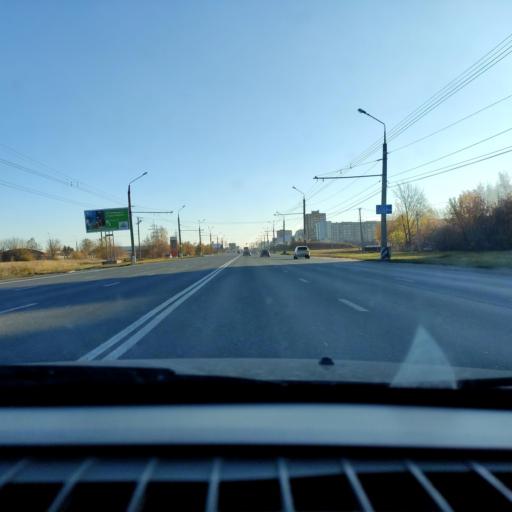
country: RU
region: Samara
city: Tol'yatti
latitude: 53.5501
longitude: 49.3250
